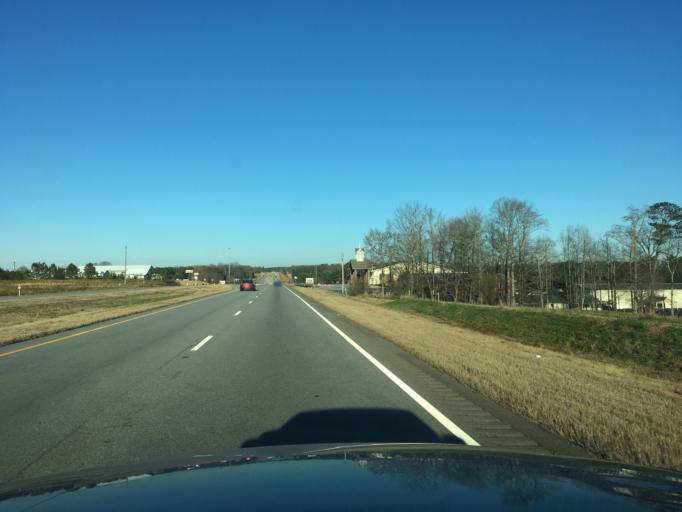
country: US
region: Georgia
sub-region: Carroll County
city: Carrollton
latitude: 33.4739
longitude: -85.1109
